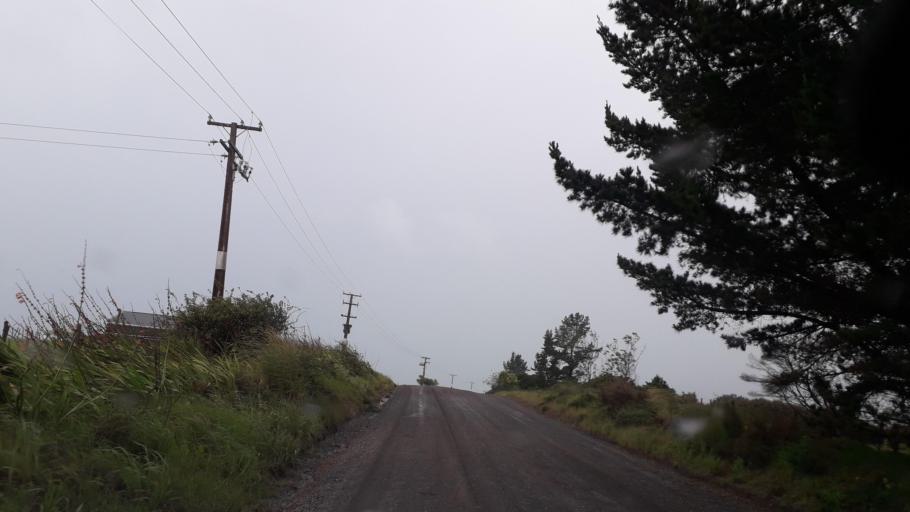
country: NZ
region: Northland
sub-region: Far North District
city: Kerikeri
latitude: -35.1342
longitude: 173.9993
